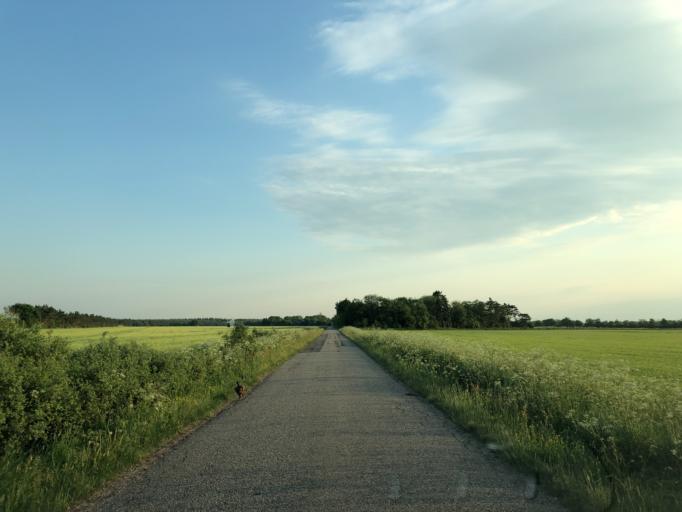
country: DK
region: Central Jutland
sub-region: Holstebro Kommune
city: Holstebro
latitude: 56.3818
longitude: 8.4648
